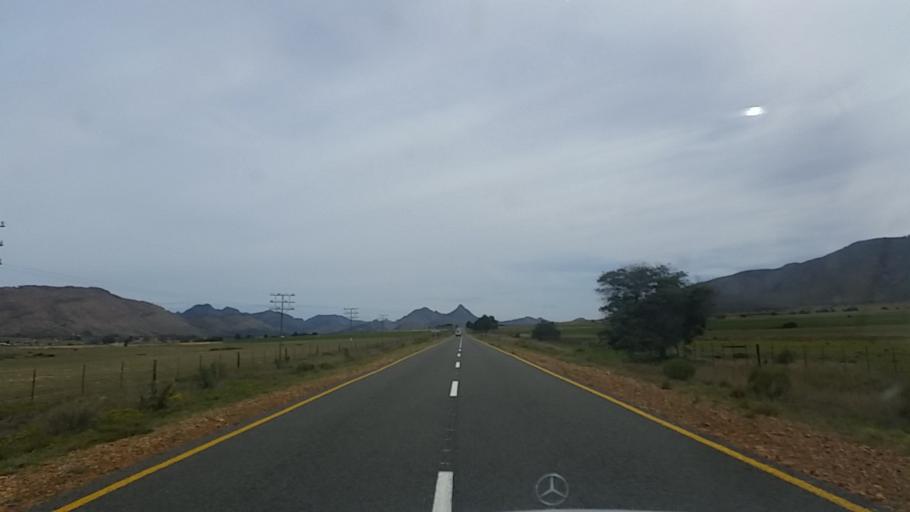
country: ZA
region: Western Cape
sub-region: Eden District Municipality
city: George
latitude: -33.8136
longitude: 22.5266
